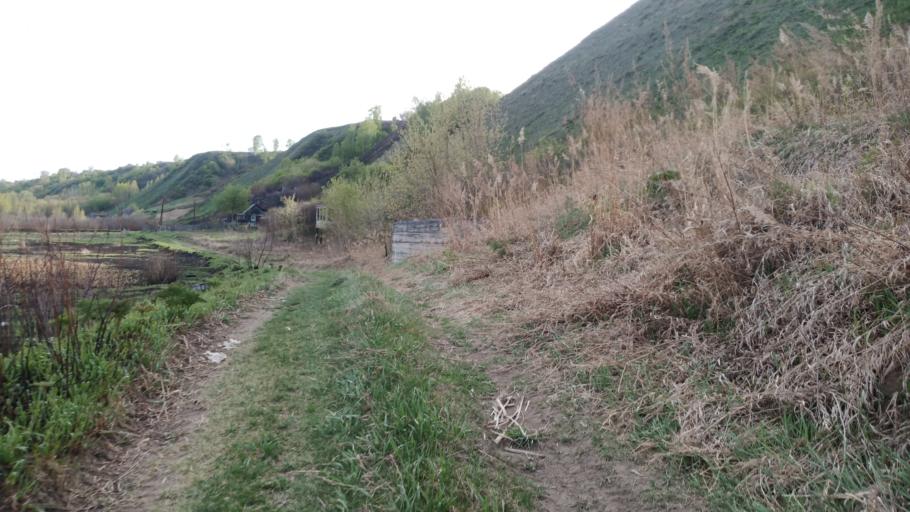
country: RU
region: Altai Krai
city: Yuzhnyy
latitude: 53.2222
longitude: 83.7250
